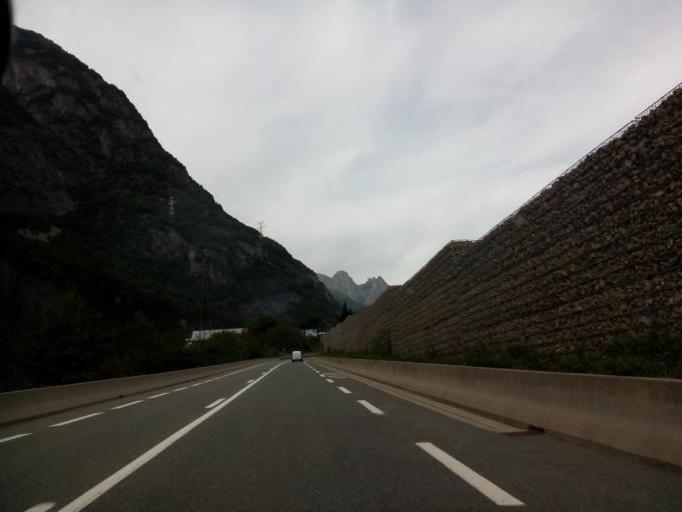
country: FR
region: Rhone-Alpes
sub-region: Departement de l'Isere
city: Vaulnaveys-le-Bas
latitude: 45.0706
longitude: 5.8714
